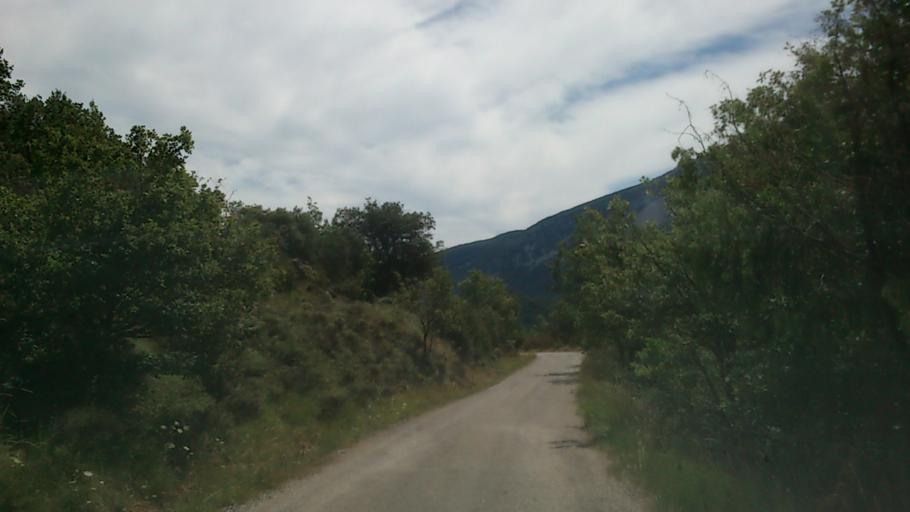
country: ES
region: Aragon
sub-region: Provincia de Huesca
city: Loporzano
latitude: 42.3176
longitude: -0.2710
